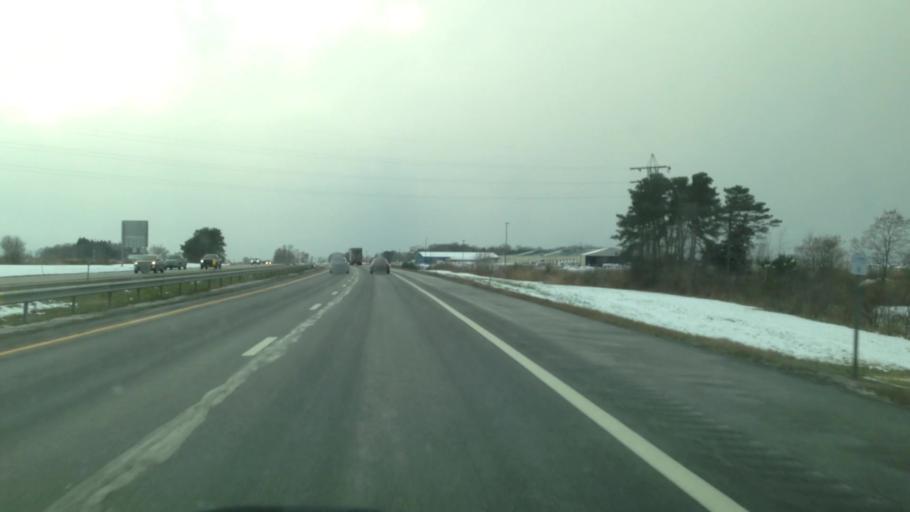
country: US
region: New York
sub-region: Montgomery County
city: Amsterdam
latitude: 42.9320
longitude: -74.2383
